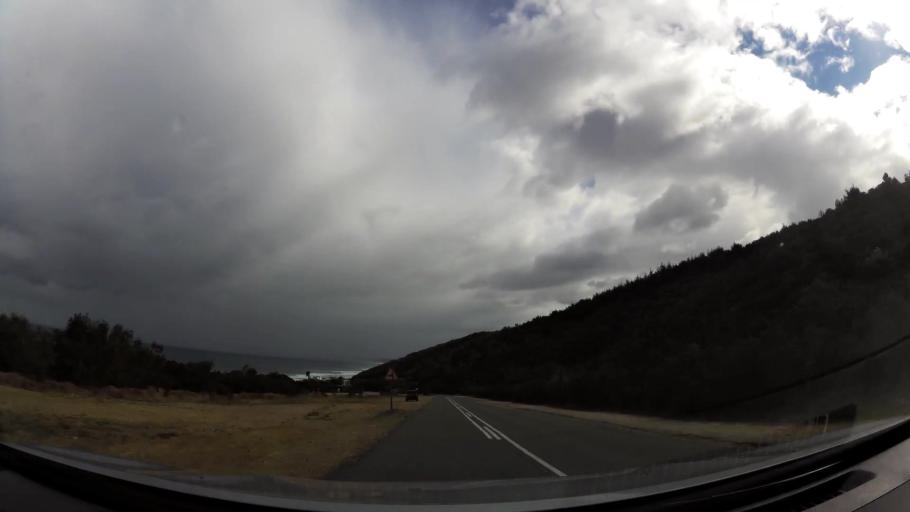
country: ZA
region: Western Cape
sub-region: Eden District Municipality
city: George
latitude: -34.0460
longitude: 22.3151
